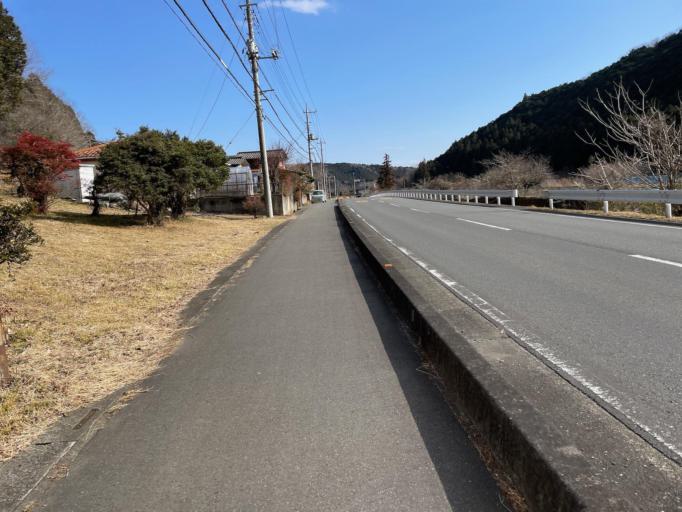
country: JP
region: Saitama
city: Hanno
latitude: 35.8435
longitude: 139.2691
